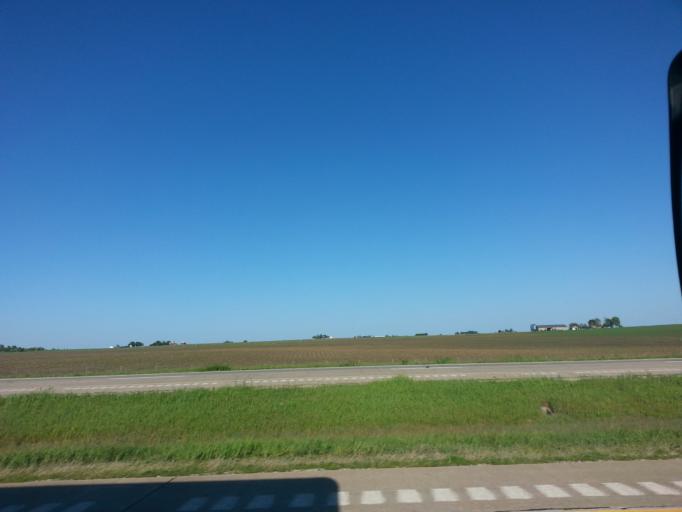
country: US
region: Illinois
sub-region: Woodford County
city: El Paso
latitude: 40.7751
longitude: -89.0350
